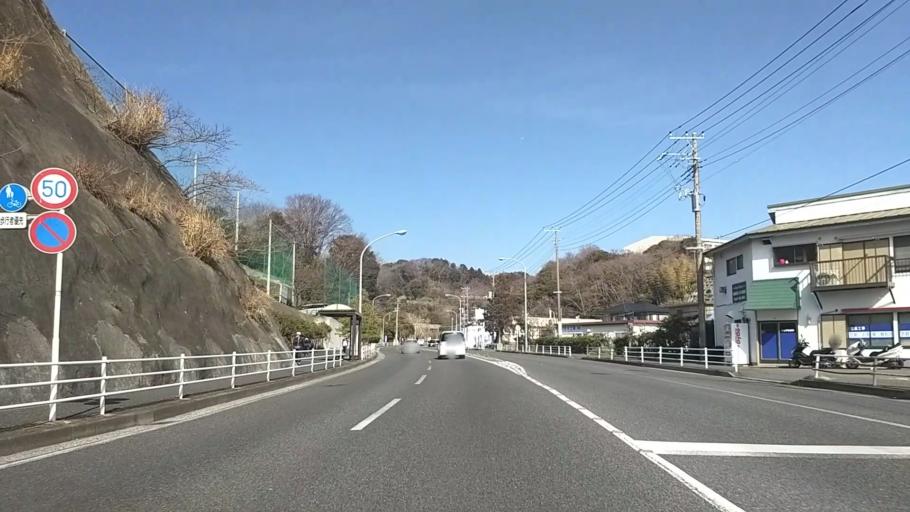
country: JP
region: Kanagawa
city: Zushi
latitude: 35.3487
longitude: 139.6080
